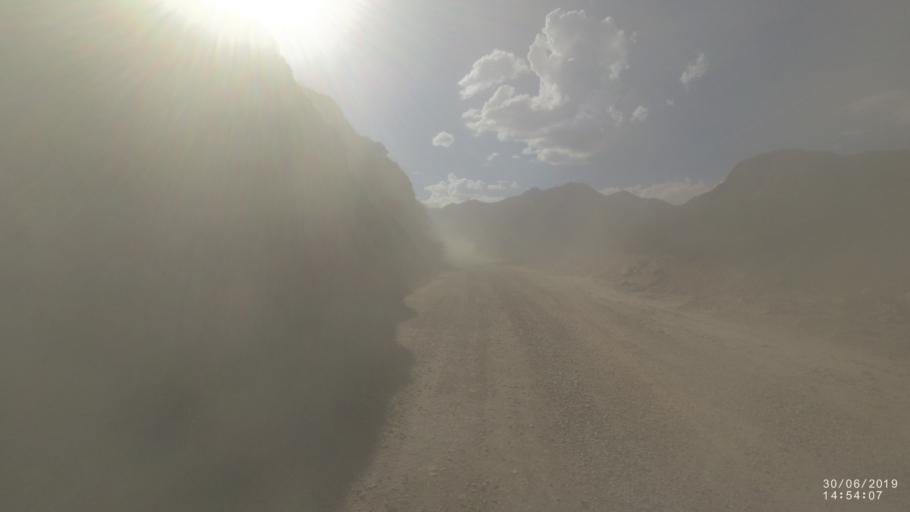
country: BO
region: Cochabamba
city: Irpa Irpa
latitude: -17.7604
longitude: -66.3495
